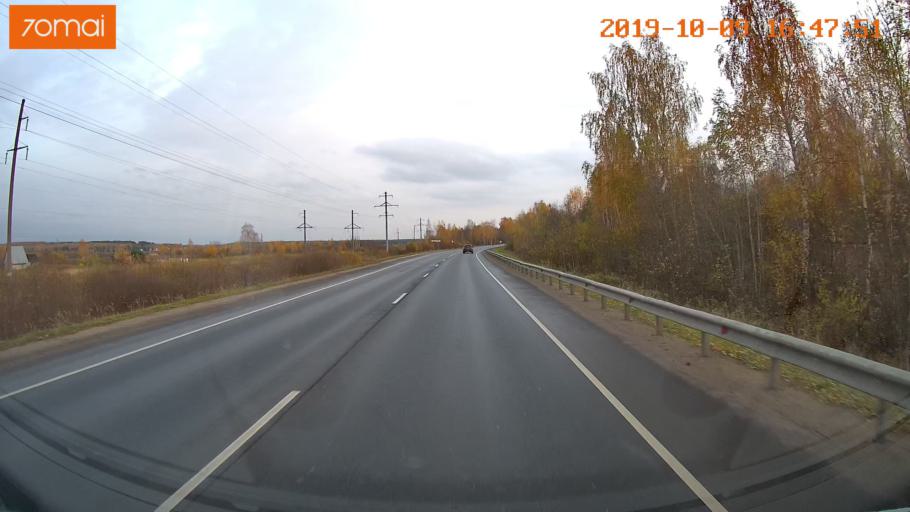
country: RU
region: Kostroma
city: Volgorechensk
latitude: 57.4342
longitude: 41.1835
